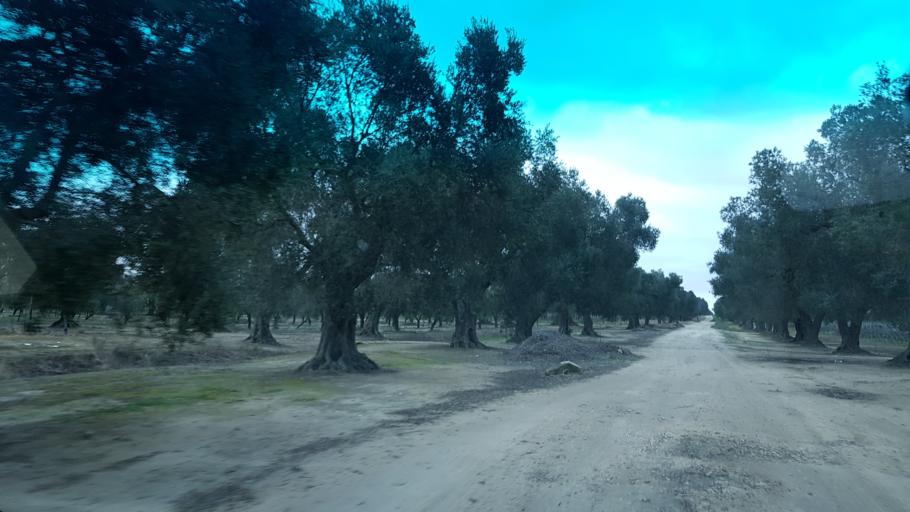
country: IT
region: Apulia
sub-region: Provincia di Brindisi
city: La Rosa
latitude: 40.5893
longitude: 17.9832
